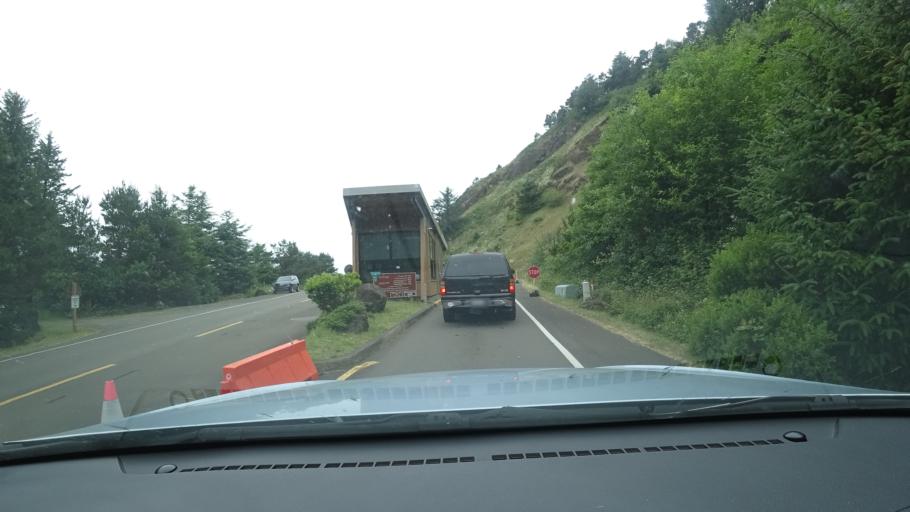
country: US
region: Oregon
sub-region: Lincoln County
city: Newport
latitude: 44.6752
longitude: -124.0653
